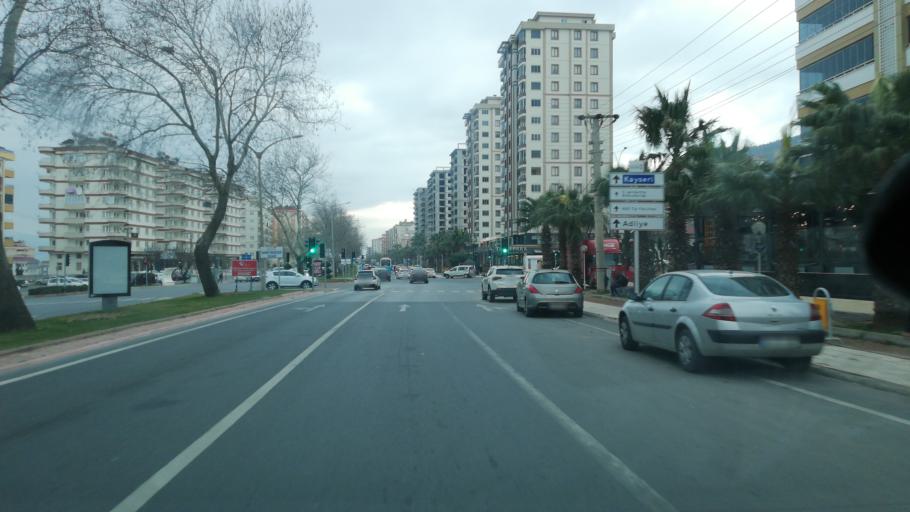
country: TR
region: Kahramanmaras
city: Kahramanmaras
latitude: 37.5915
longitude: 36.8689
